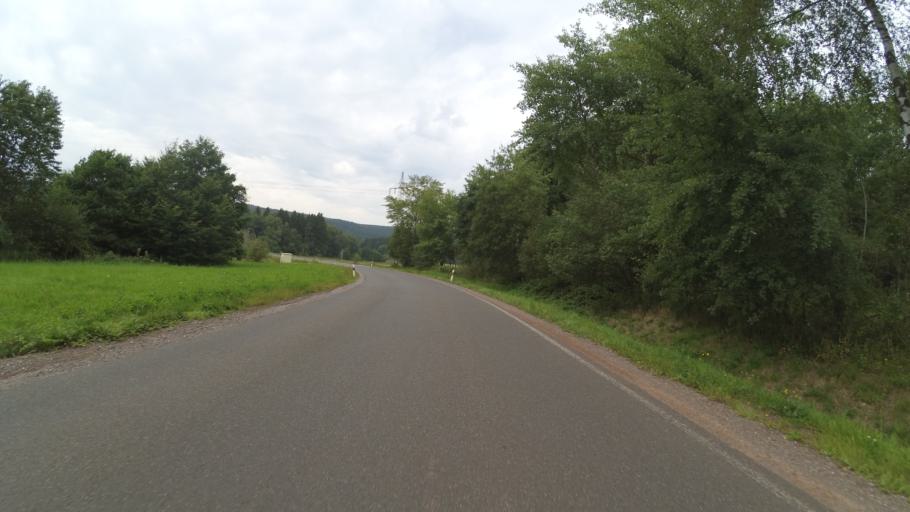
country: DE
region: Rheinland-Pfalz
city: Greimerath
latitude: 49.5629
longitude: 6.6683
